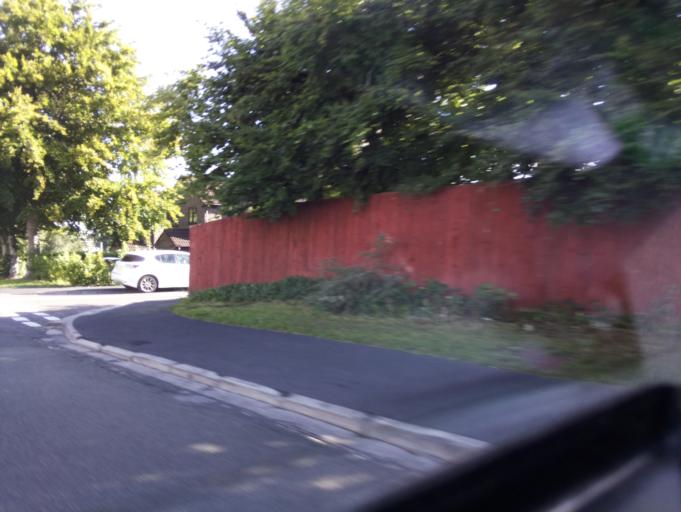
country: GB
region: England
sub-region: Bath and North East Somerset
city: Whitchurch
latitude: 51.4240
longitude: -2.5568
